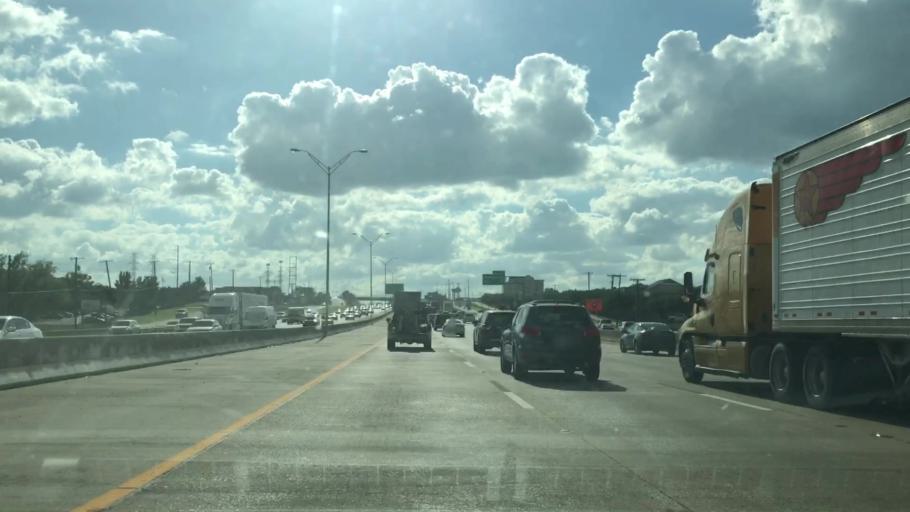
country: US
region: Texas
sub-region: Dallas County
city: Sunnyvale
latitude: 32.8365
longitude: -96.6047
